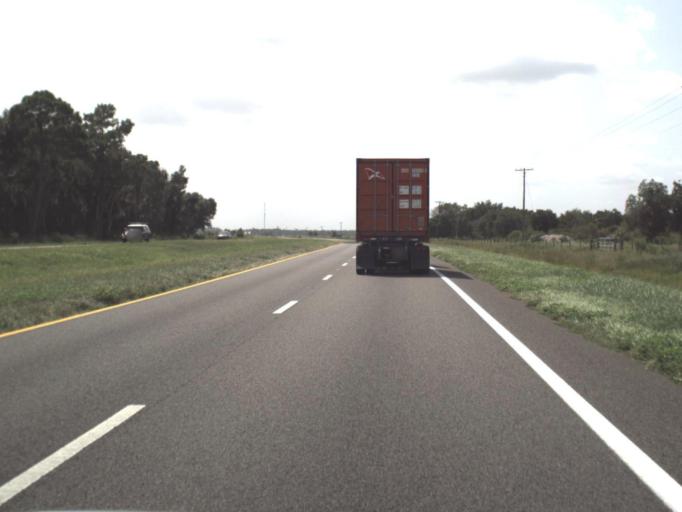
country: US
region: Florida
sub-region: Polk County
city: Crooked Lake Park
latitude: 27.8162
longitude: -81.5969
